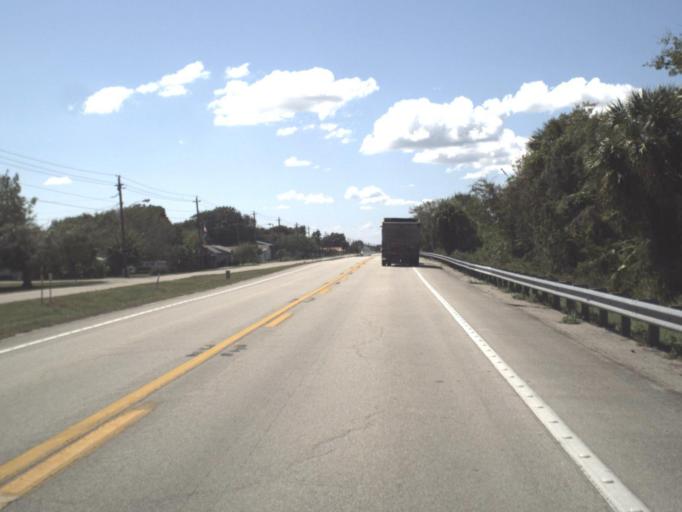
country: US
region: Florida
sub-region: Glades County
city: Buckhead Ridge
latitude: 27.1424
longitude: -80.8818
